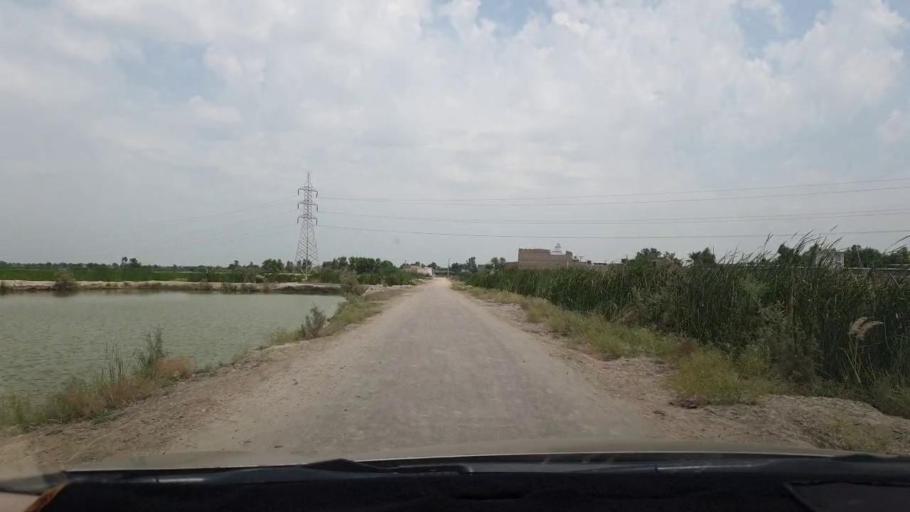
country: PK
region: Sindh
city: Naudero
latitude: 27.7237
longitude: 68.3360
